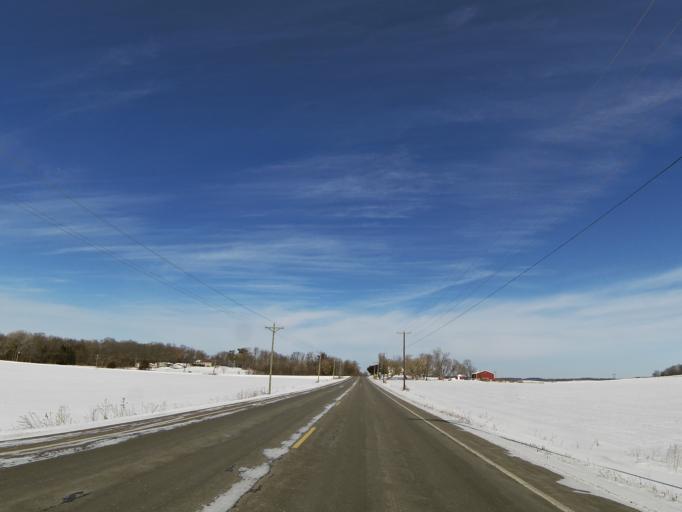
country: US
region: Minnesota
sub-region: Washington County
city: Afton
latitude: 44.8455
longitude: -92.7312
